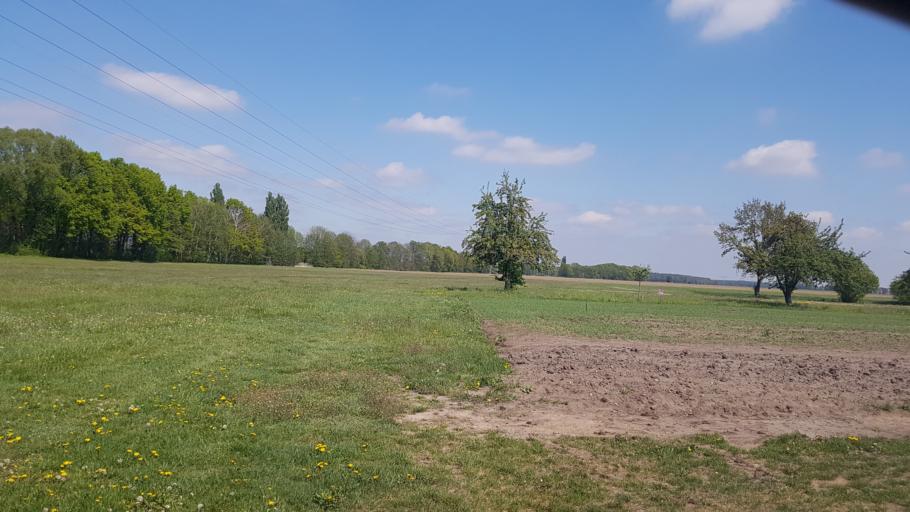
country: DE
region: Brandenburg
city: Sonnewalde
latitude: 51.6700
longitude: 13.6468
